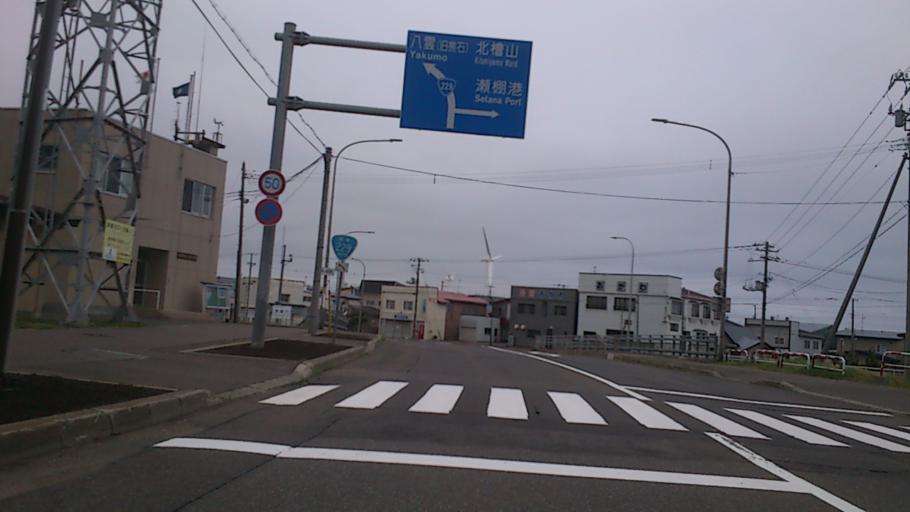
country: JP
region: Hokkaido
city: Iwanai
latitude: 42.4566
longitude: 139.8492
